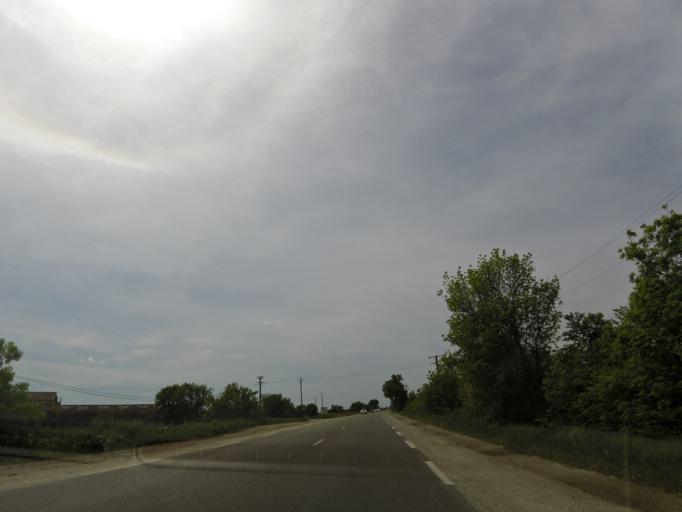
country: FR
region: Languedoc-Roussillon
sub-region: Departement de l'Herault
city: Saint-Just
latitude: 43.6399
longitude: 4.1370
